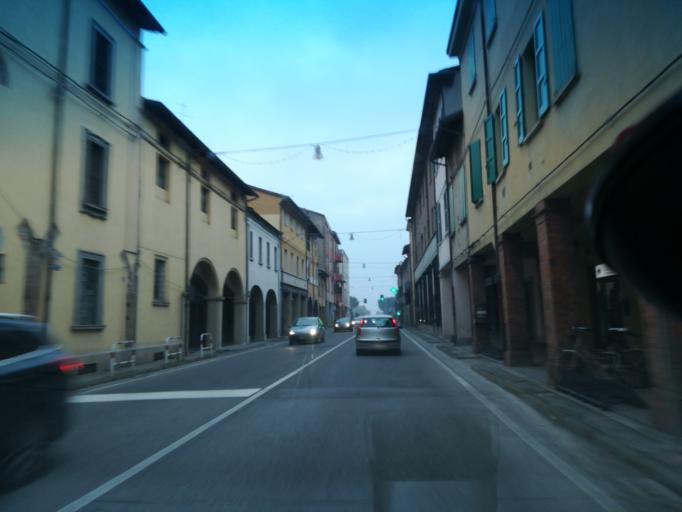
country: IT
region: Emilia-Romagna
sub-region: Provincia di Ravenna
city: Castel Bolognese
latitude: 44.3195
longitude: 11.7999
